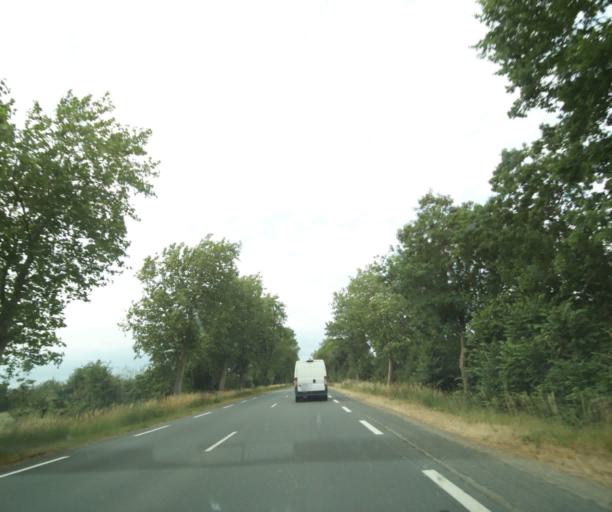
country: FR
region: Poitou-Charentes
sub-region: Departement de la Charente-Maritime
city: Andilly
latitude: 46.2738
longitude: -1.0015
